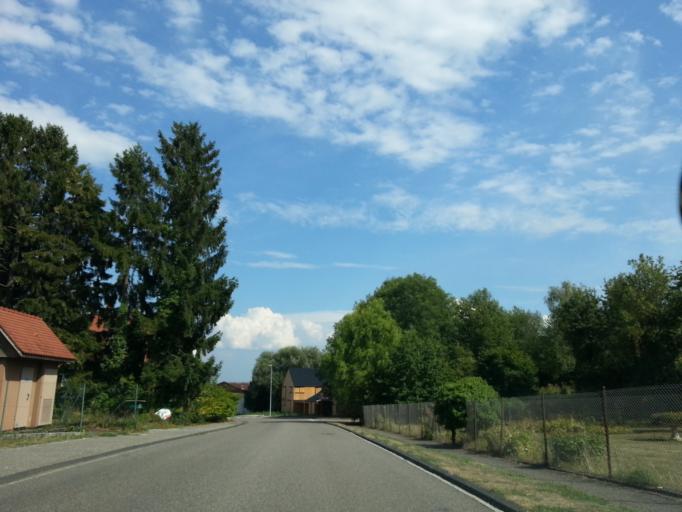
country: FR
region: Alsace
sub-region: Departement du Bas-Rhin
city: Surbourg
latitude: 48.9404
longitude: 7.8183
